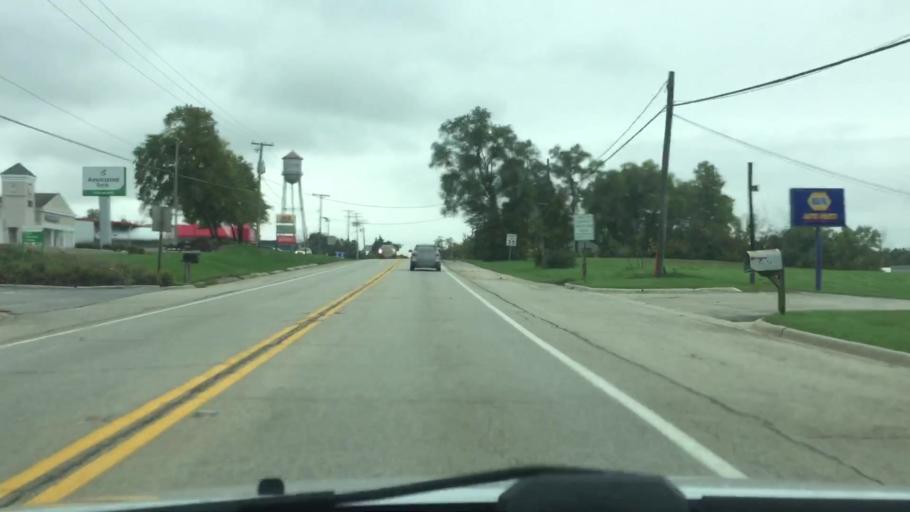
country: US
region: Illinois
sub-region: McHenry County
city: Richmond
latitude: 42.4854
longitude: -88.3061
